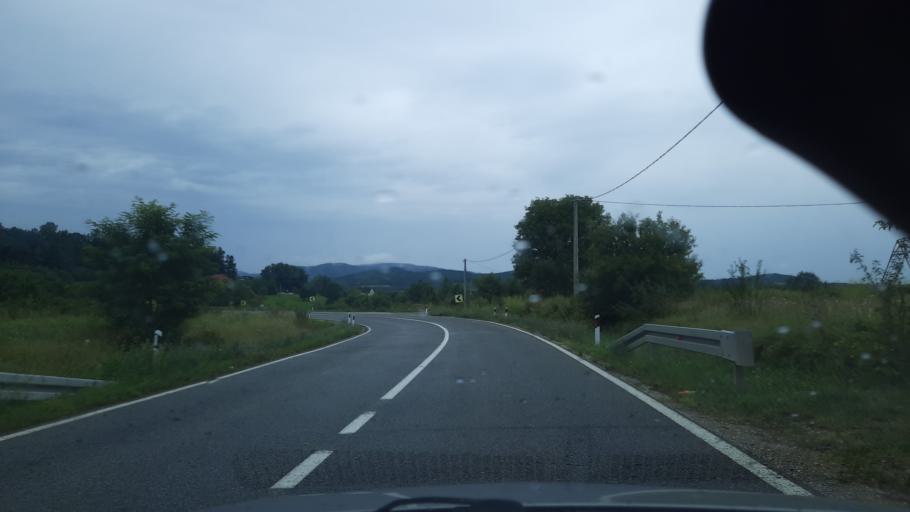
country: RS
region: Central Serbia
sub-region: Sumadijski Okrug
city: Knic
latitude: 43.9108
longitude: 20.7673
